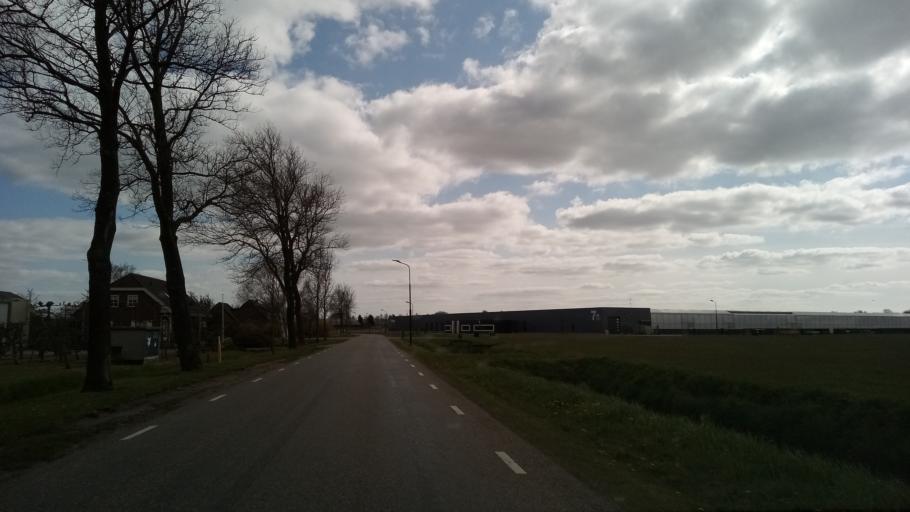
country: NL
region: North Holland
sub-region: Gemeente Heerhugowaard
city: Heerhugowaard
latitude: 52.7023
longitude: 4.8353
